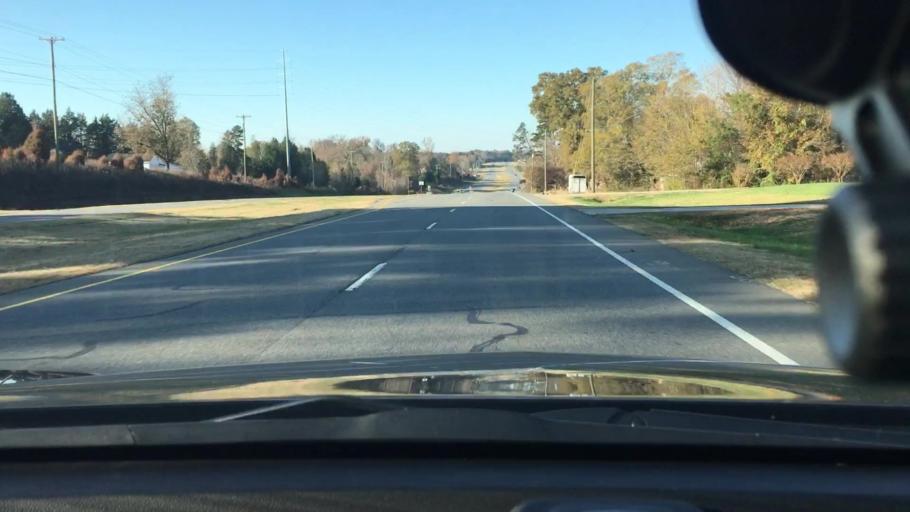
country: US
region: North Carolina
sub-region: Cabarrus County
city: Mount Pleasant
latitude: 35.3935
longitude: -80.4839
